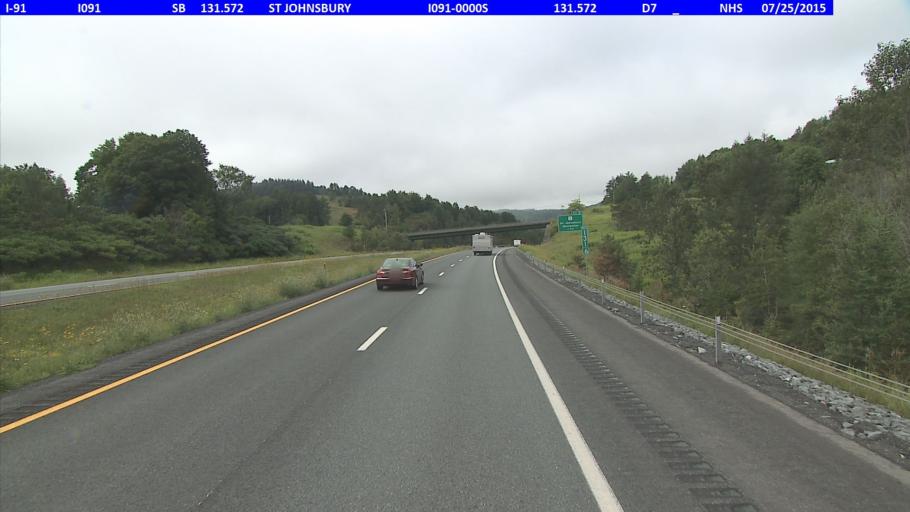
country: US
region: Vermont
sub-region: Caledonia County
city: St Johnsbury
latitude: 44.4402
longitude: -72.0262
